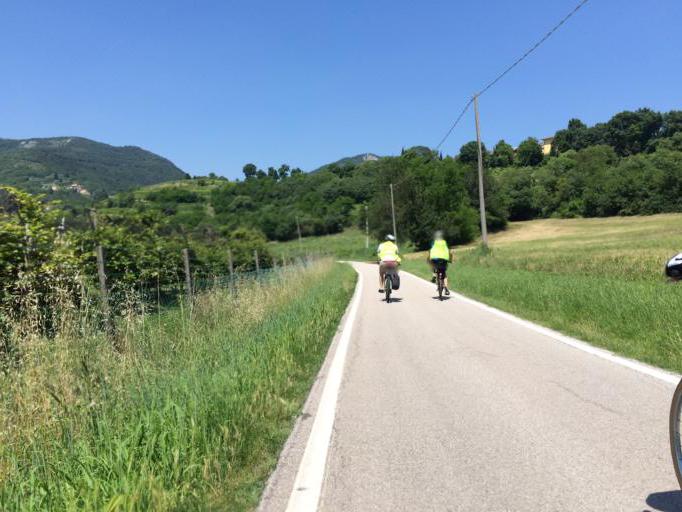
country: IT
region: Veneto
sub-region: Provincia di Vicenza
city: Barbarano Vicentino
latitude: 45.4030
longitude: 11.5484
